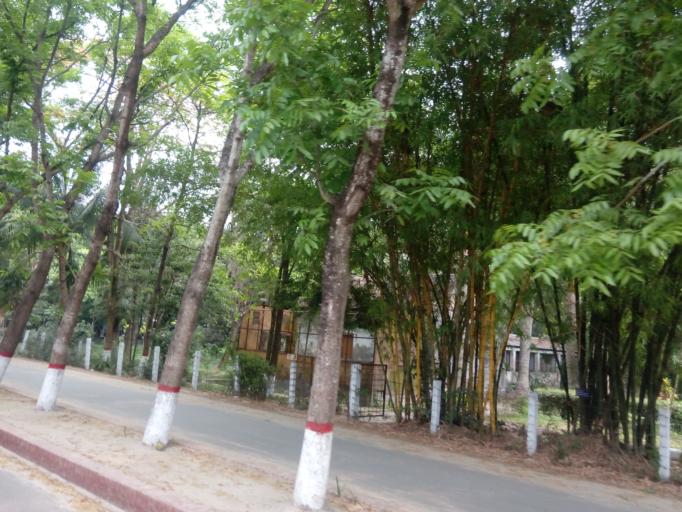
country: BD
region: Khulna
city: Khulna
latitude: 22.8009
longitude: 89.5342
